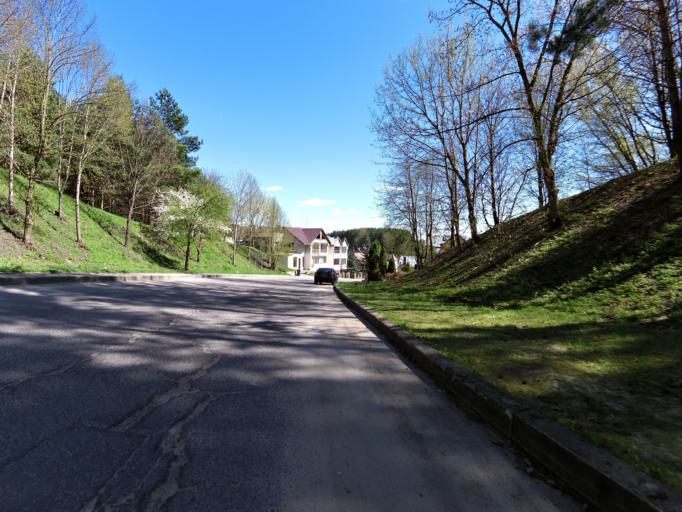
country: LT
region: Vilnius County
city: Rasos
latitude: 54.6885
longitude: 25.3147
